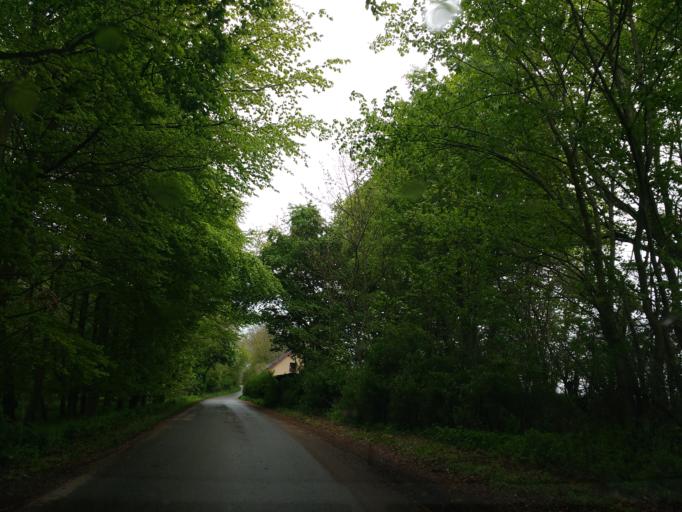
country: DE
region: Schleswig-Holstein
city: Waabs
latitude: 54.5417
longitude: 10.0077
